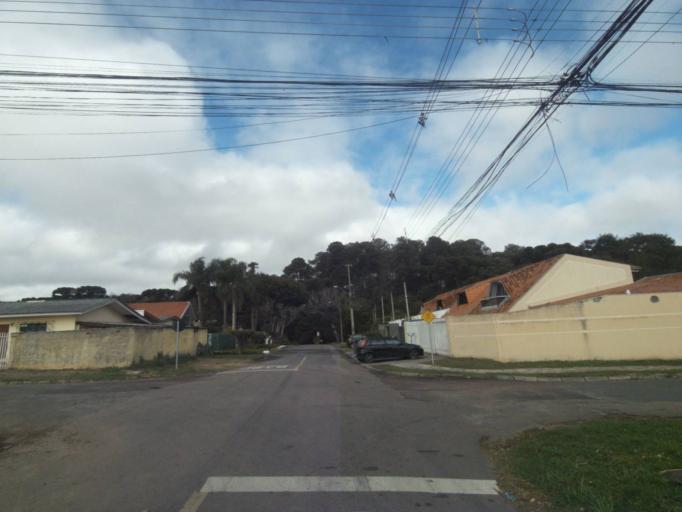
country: BR
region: Parana
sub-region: Sao Jose Dos Pinhais
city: Sao Jose dos Pinhais
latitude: -25.5239
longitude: -49.3028
